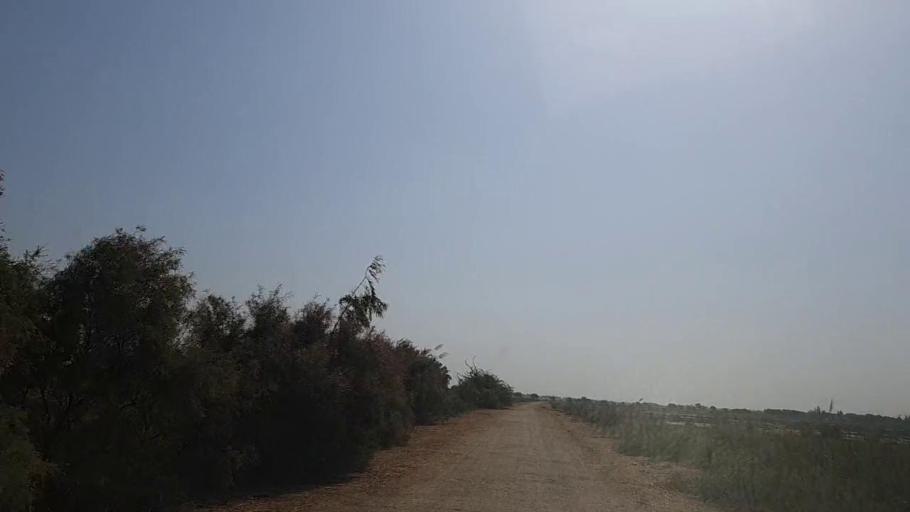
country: PK
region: Sindh
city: Daro Mehar
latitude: 24.7107
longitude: 68.1231
